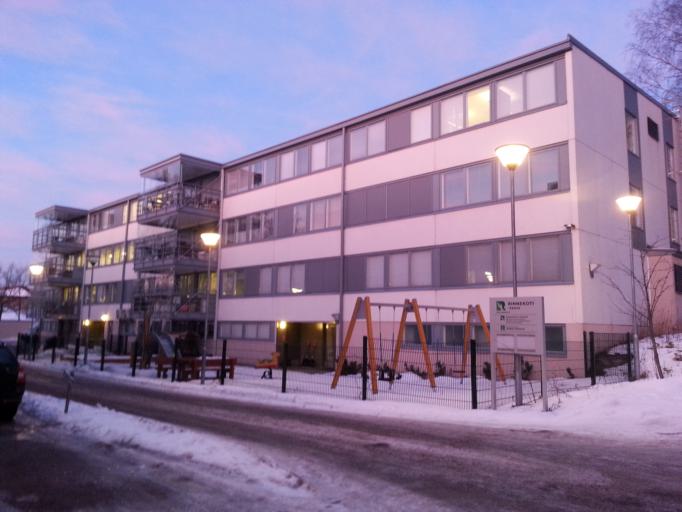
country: FI
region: Uusimaa
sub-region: Helsinki
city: Teekkarikylae
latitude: 60.2164
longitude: 24.8744
